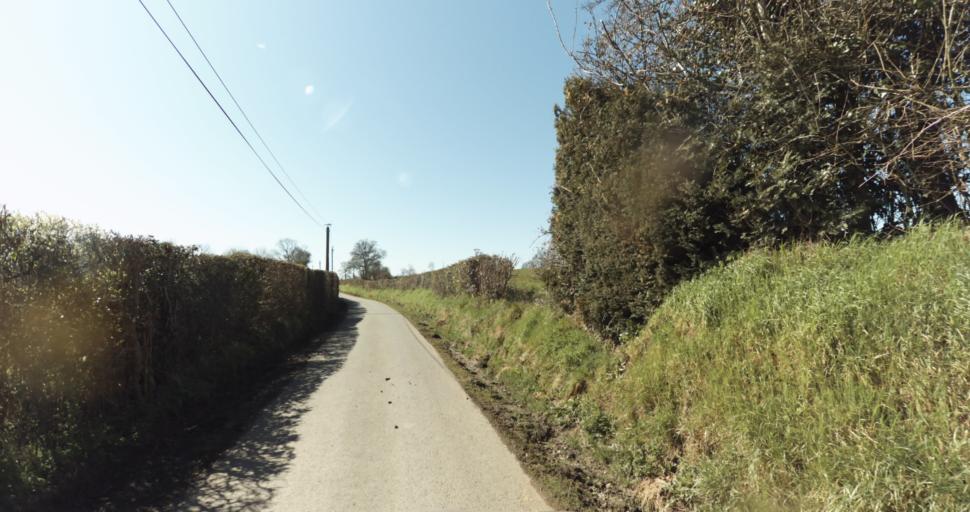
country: FR
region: Lower Normandy
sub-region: Departement du Calvados
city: Livarot
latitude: 48.9891
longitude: 0.1120
